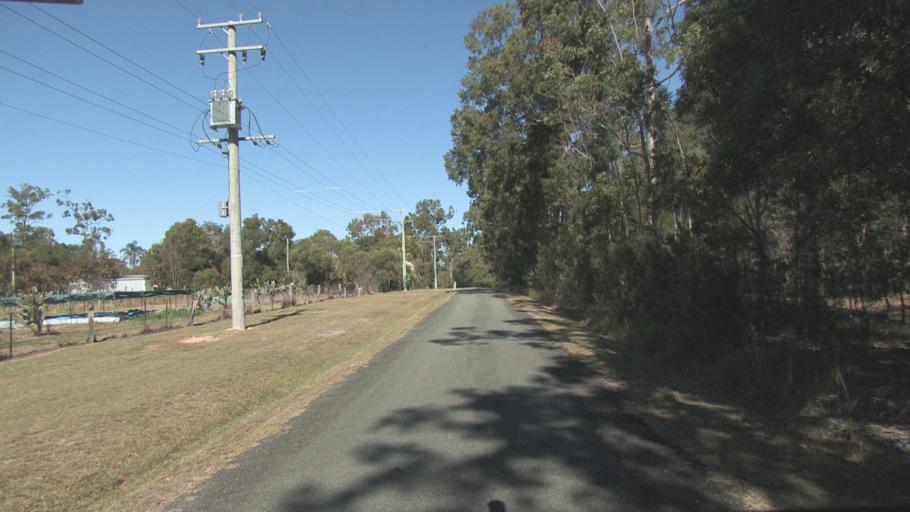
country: AU
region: Queensland
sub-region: Logan
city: Park Ridge South
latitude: -27.7006
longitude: 153.0036
